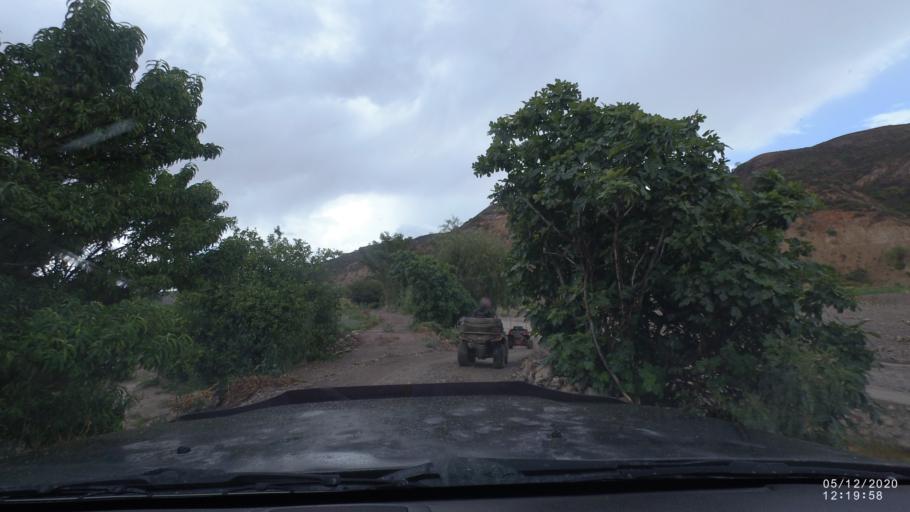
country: BO
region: Cochabamba
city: Sipe Sipe
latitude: -17.5546
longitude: -66.3877
